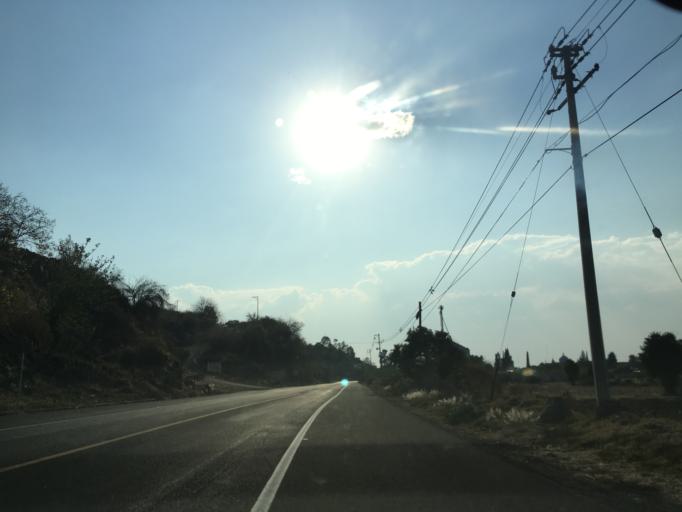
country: MX
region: Michoacan
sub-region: Indaparapeo
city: Colonia de Guadalupe
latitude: 19.8065
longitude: -100.8763
